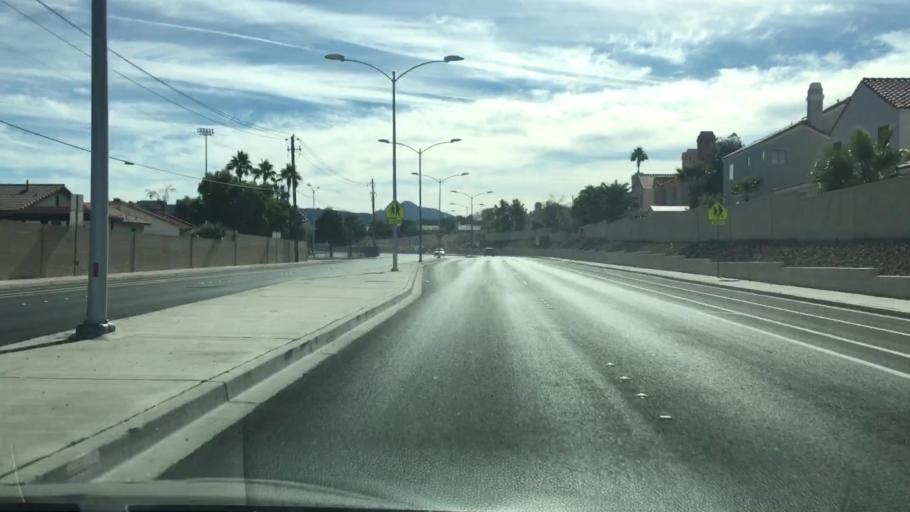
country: US
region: Nevada
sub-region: Clark County
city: Whitney
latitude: 36.0608
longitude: -115.0587
